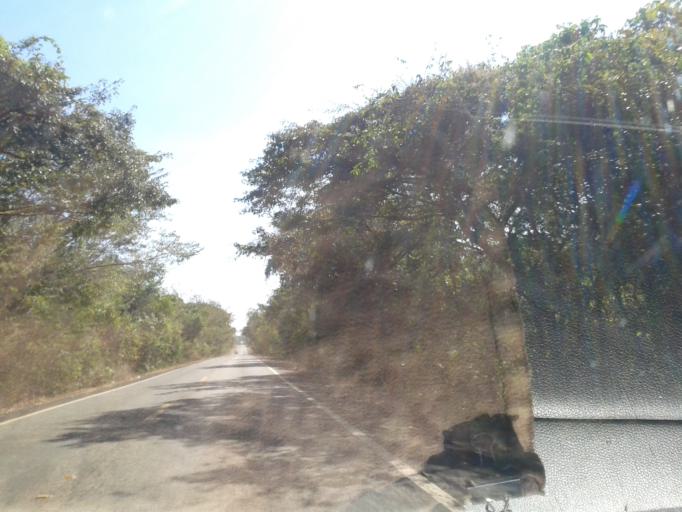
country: BR
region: Goias
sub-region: Crixas
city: Crixas
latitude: -13.9586
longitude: -50.3201
